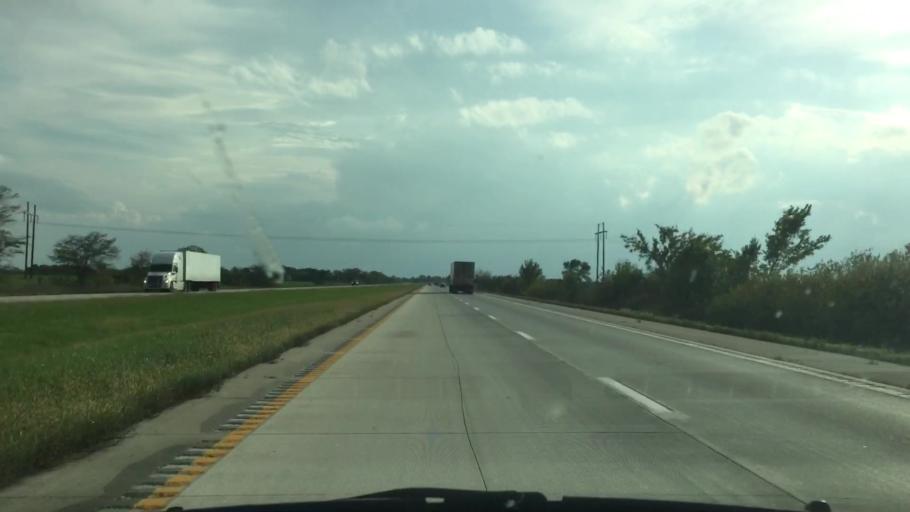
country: US
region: Missouri
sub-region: Daviess County
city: Gallatin
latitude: 39.9639
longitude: -94.1003
